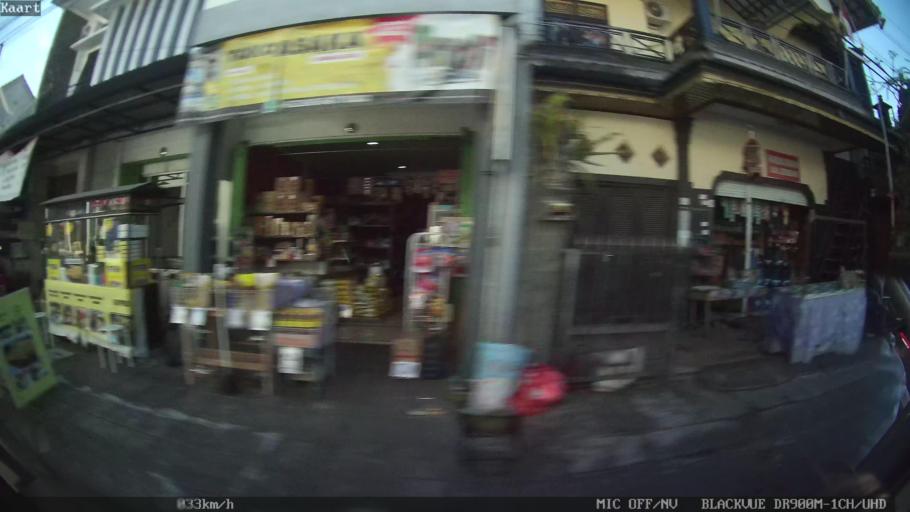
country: ID
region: Bali
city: Banjar Gunungpande
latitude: -8.6301
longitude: 115.1686
